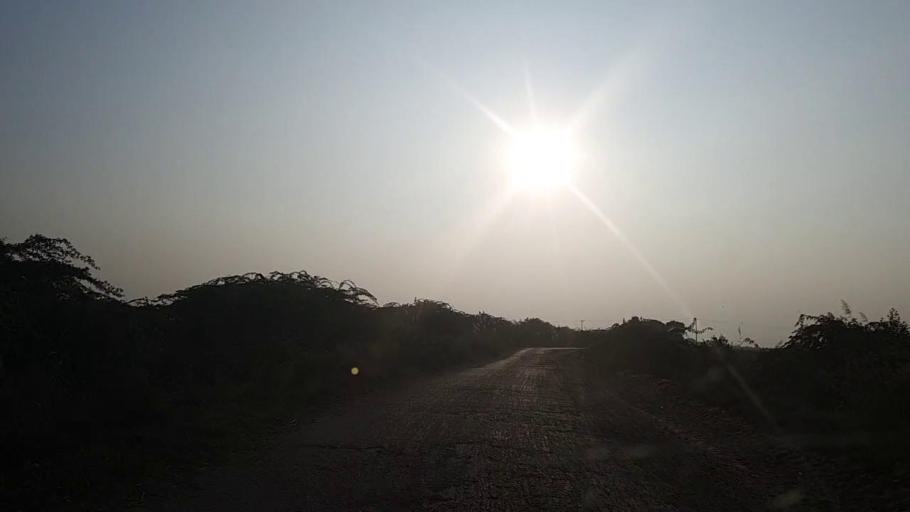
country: PK
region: Sindh
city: Mirpur Sakro
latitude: 24.5626
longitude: 67.6143
